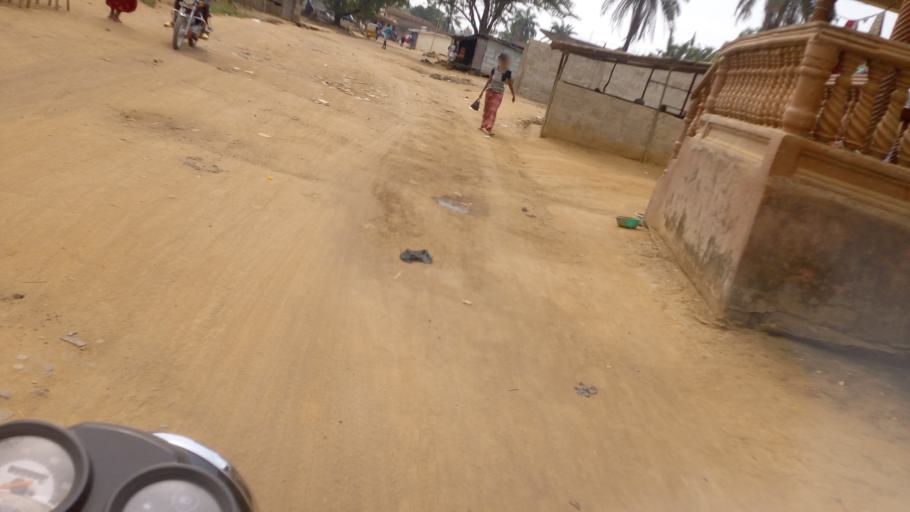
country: SL
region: Western Area
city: Waterloo
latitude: 8.3268
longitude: -13.0571
